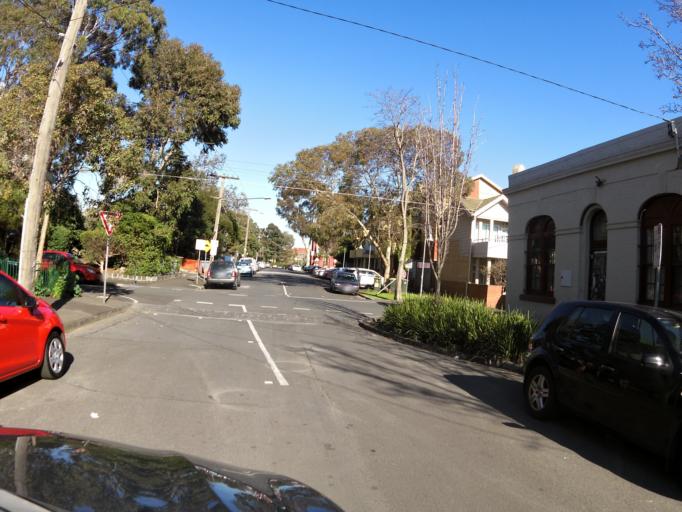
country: AU
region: Victoria
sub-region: Yarra
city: Clifton Hill
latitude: -37.8003
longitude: 144.9909
